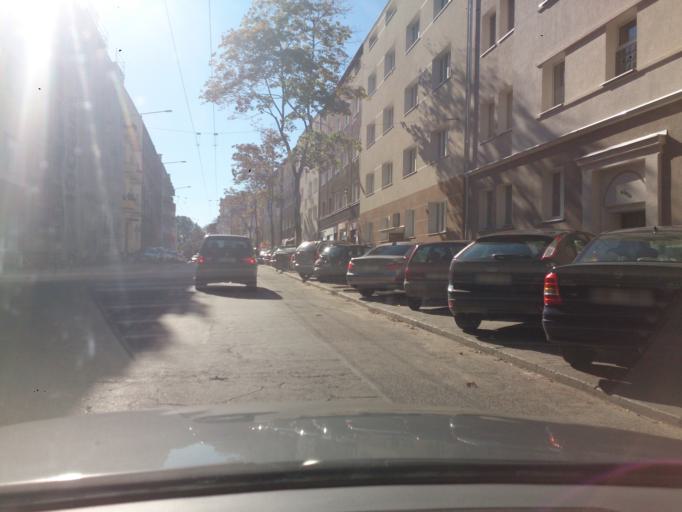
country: PL
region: Pomeranian Voivodeship
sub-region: Gdynia
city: Gdynia
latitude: 54.5144
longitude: 18.5315
